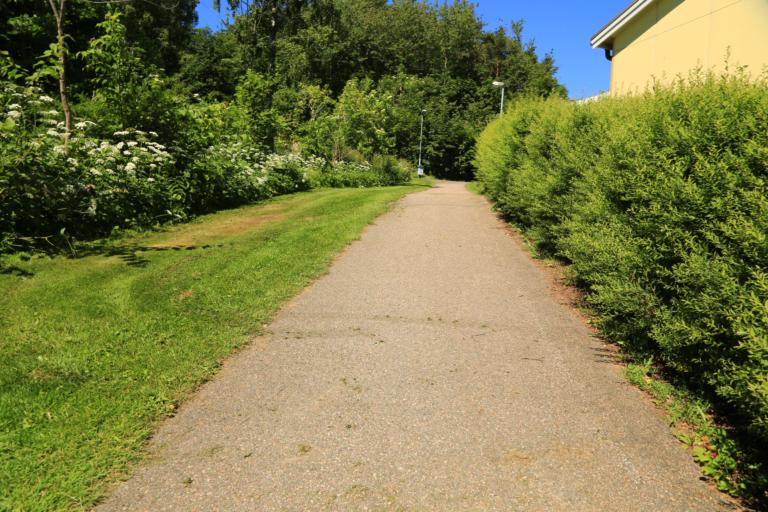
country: SE
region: Halland
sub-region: Varbergs Kommun
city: Varberg
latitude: 57.1131
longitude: 12.2706
